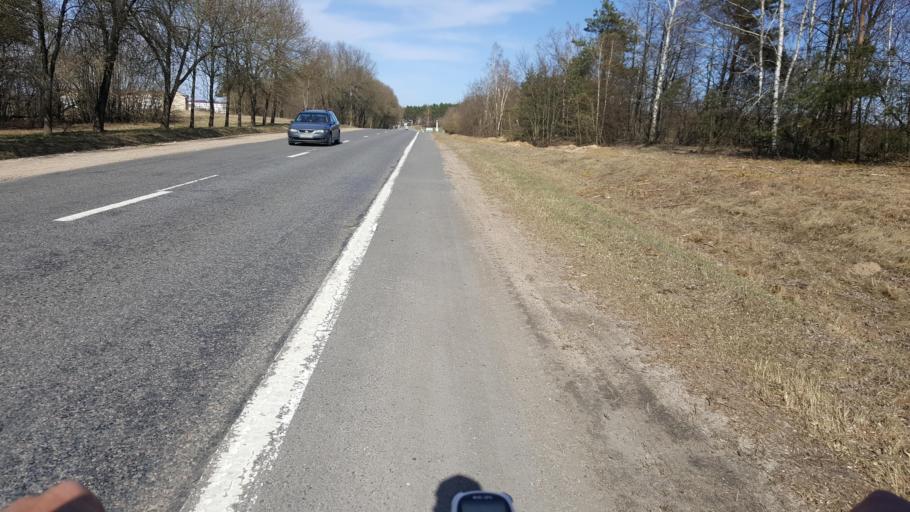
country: BY
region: Brest
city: Kamyanyets
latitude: 52.3843
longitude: 23.8132
